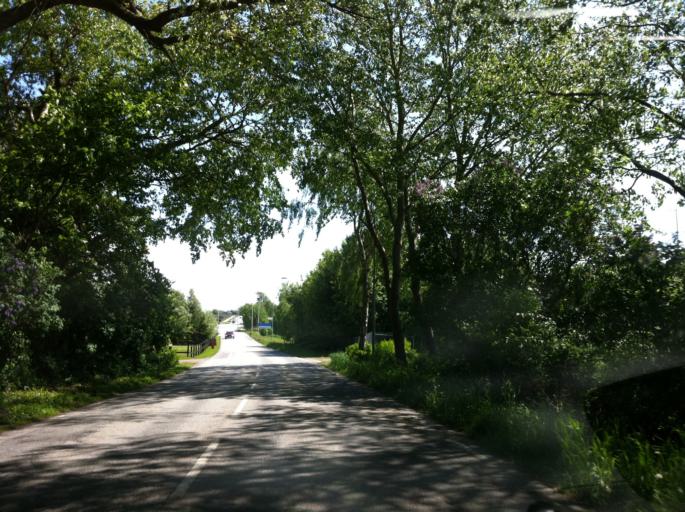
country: SE
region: Skane
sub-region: Kavlinge Kommun
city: Hofterup
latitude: 55.7976
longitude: 12.9906
